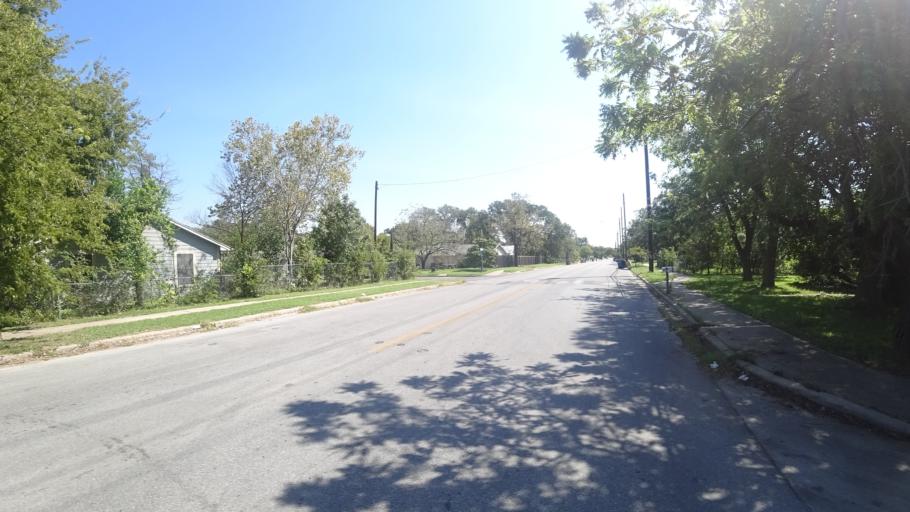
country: US
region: Texas
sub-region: Travis County
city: Austin
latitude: 30.3101
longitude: -97.6829
